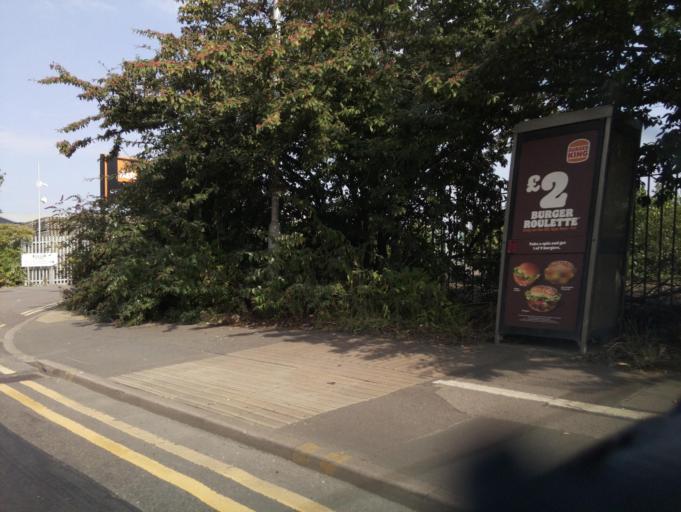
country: GB
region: England
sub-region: Staffordshire
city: Burton upon Trent
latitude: 52.8024
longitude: -1.6517
